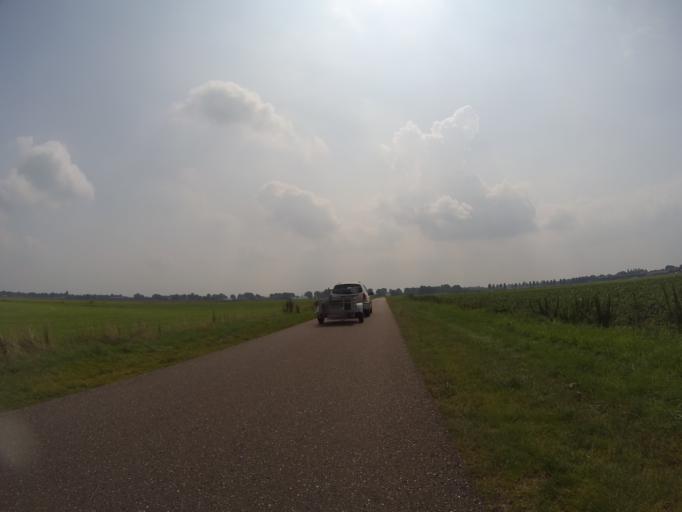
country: NL
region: Drenthe
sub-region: Gemeente Emmen
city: Emmer-Compascuum
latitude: 52.8024
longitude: 7.0255
